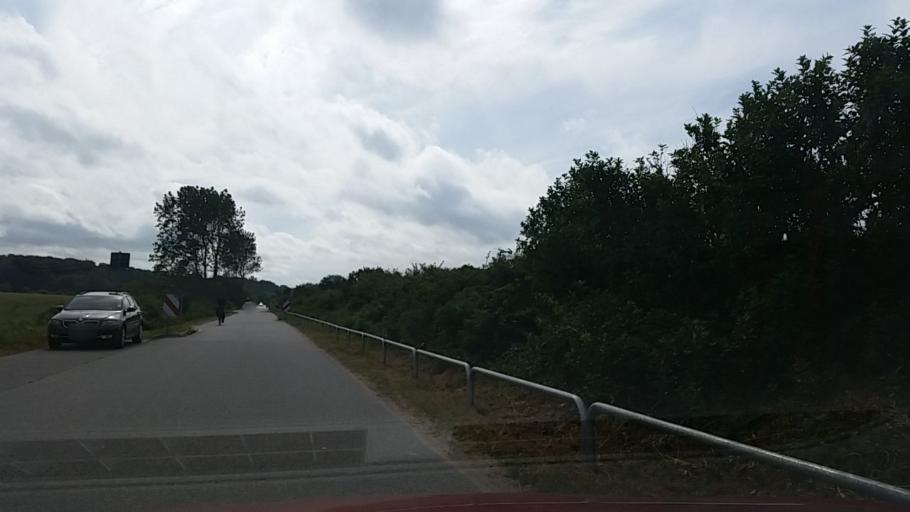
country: DE
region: Mecklenburg-Vorpommern
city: Bad Doberan
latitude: 54.1463
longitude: 11.8629
